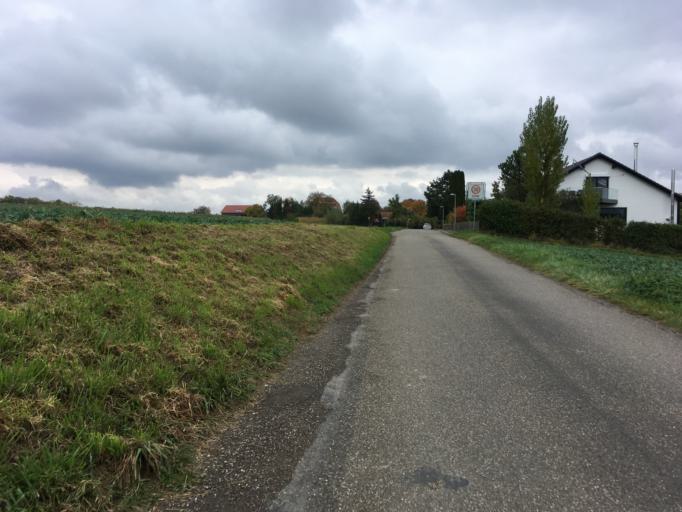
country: DE
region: Baden-Wuerttemberg
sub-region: Tuebingen Region
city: Dusslingen
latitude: 48.4784
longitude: 9.0533
